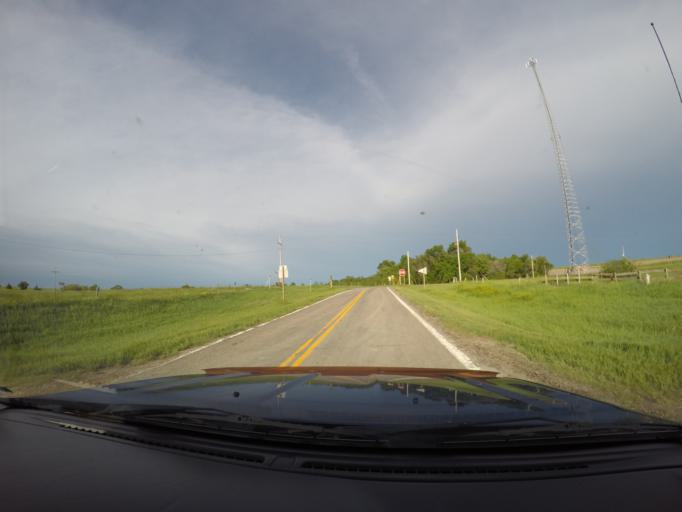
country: US
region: Kansas
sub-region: Smith County
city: Smith Center
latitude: 39.8282
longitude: -98.5612
